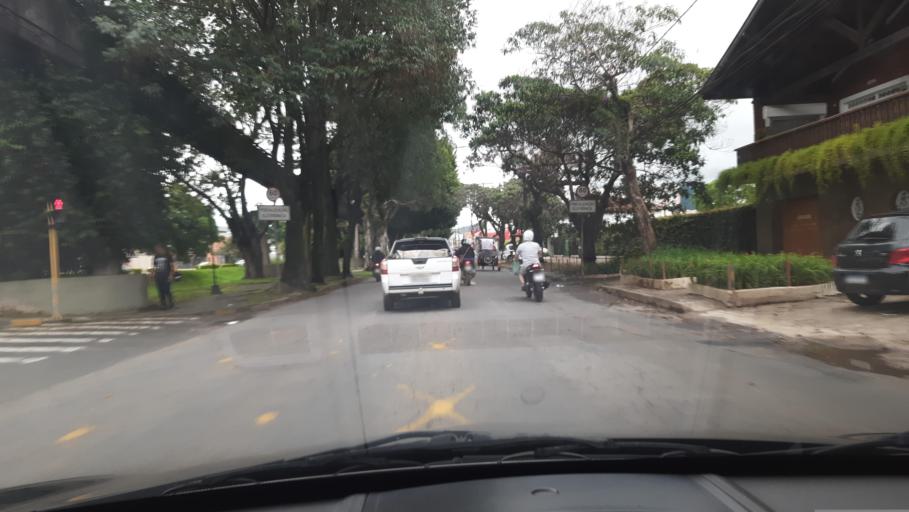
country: BR
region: Minas Gerais
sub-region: Pocos De Caldas
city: Pocos de Caldas
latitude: -21.7854
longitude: -46.5808
